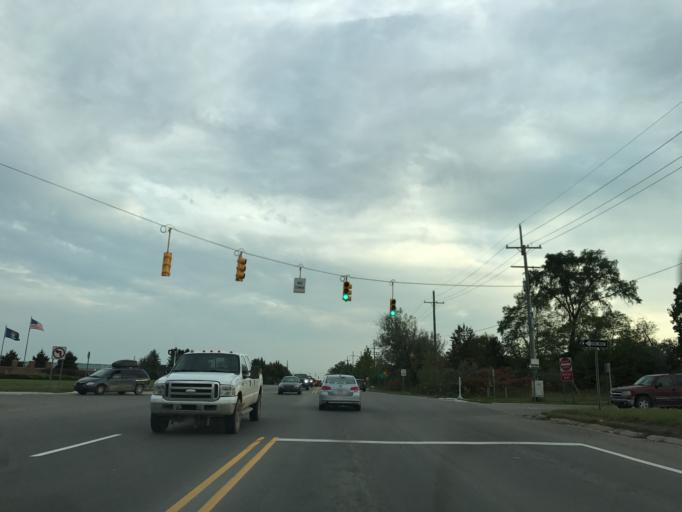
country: US
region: Michigan
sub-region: Oakland County
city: South Lyon
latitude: 42.5178
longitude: -83.6163
